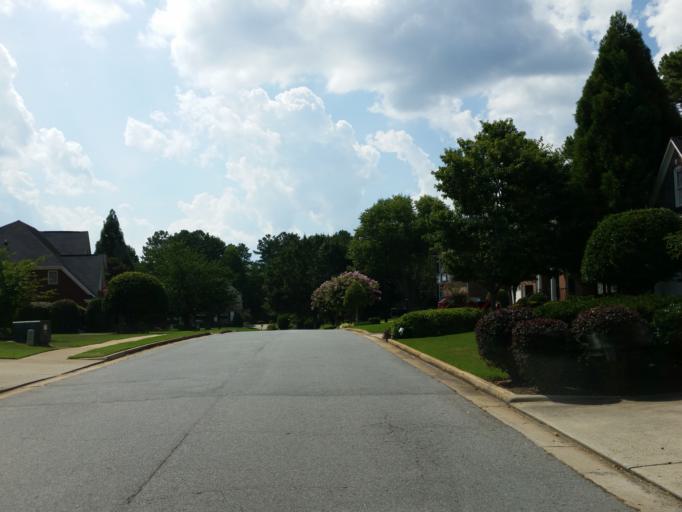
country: US
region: Georgia
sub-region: Cherokee County
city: Woodstock
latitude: 34.0361
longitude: -84.4682
